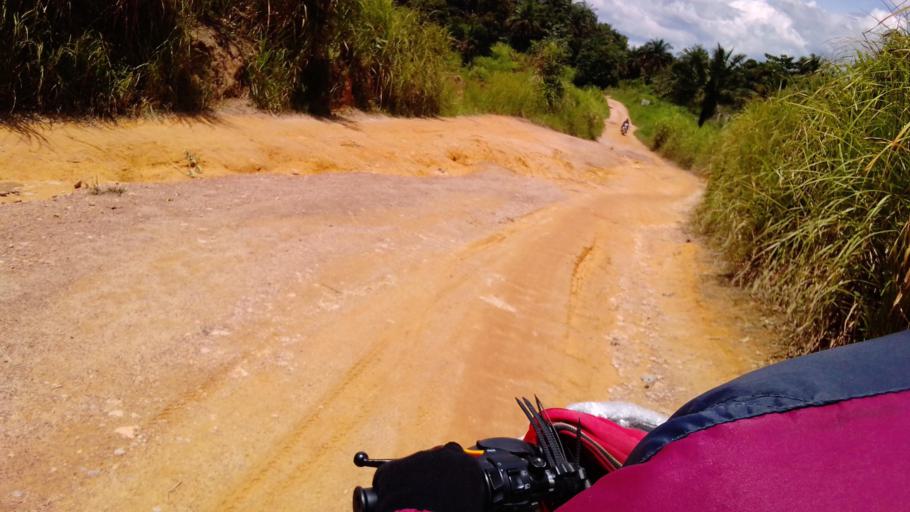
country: SL
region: Eastern Province
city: Koidu
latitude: 8.6875
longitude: -10.9560
